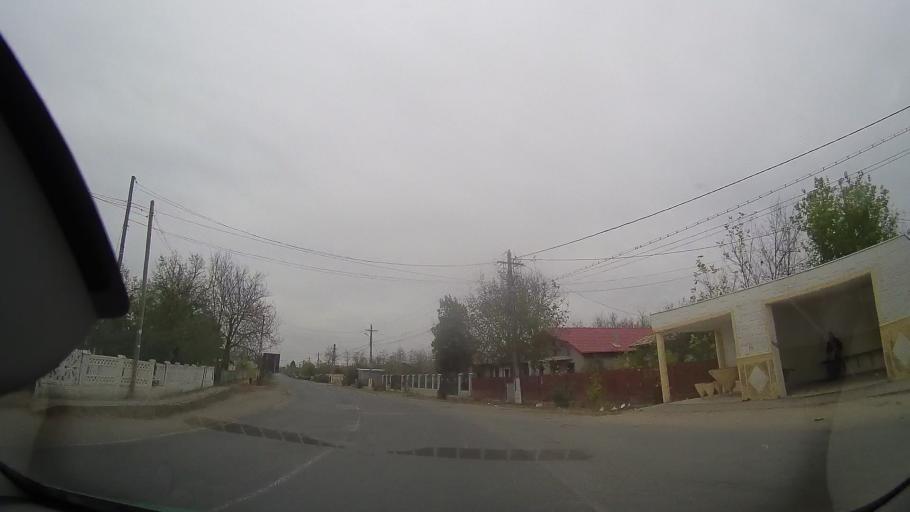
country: RO
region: Ialomita
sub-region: Comuna Grivita
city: Grivita
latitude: 44.7321
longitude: 27.2990
